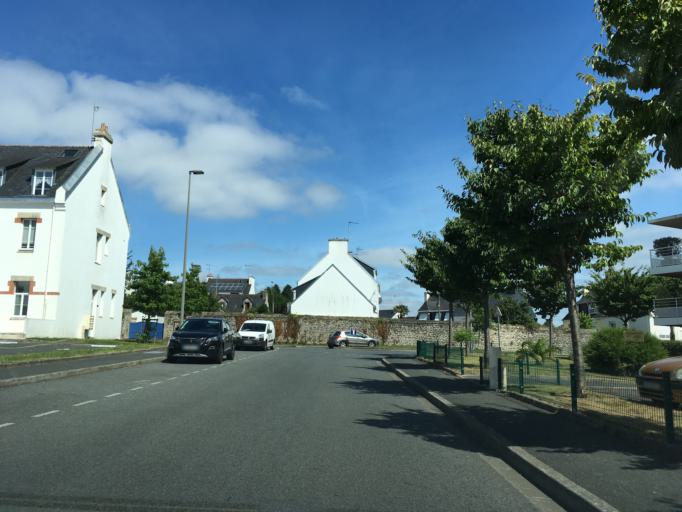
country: FR
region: Brittany
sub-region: Departement du Finistere
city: Quimper
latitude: 48.0070
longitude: -4.0939
